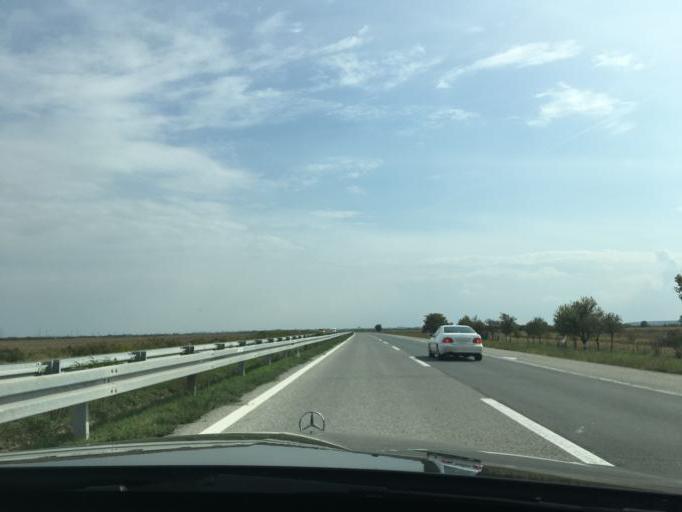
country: RS
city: Ravnje
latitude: 45.0245
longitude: 19.4852
